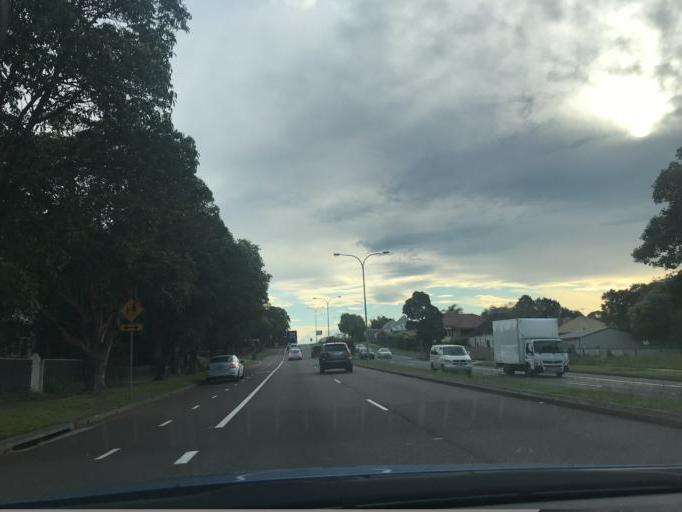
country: AU
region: New South Wales
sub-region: Newcastle
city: Elermore Vale
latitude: -32.9050
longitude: 151.6737
